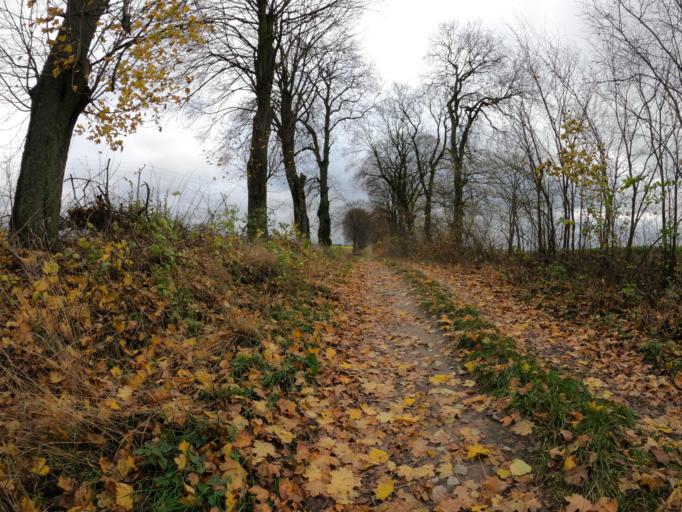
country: PL
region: West Pomeranian Voivodeship
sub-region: Powiat walecki
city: Tuczno
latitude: 53.2548
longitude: 16.1986
